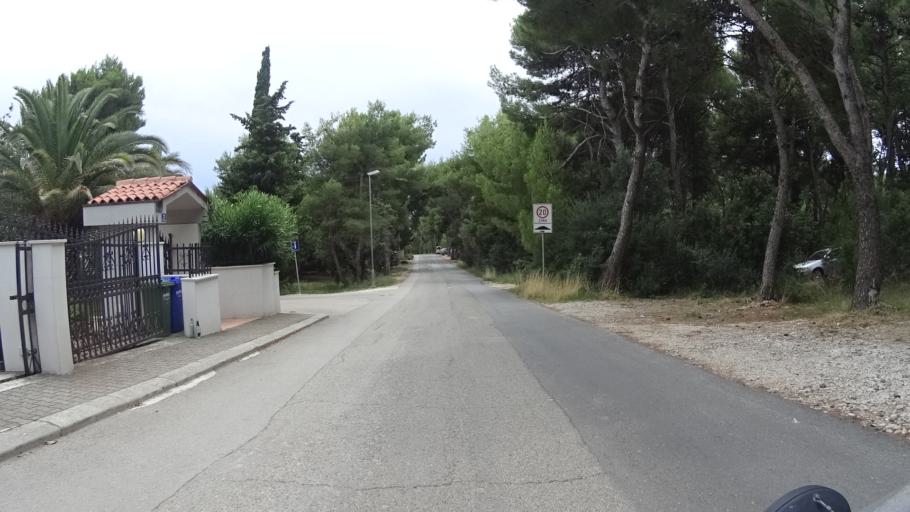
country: HR
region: Istarska
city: Medulin
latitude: 44.8035
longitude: 13.9068
